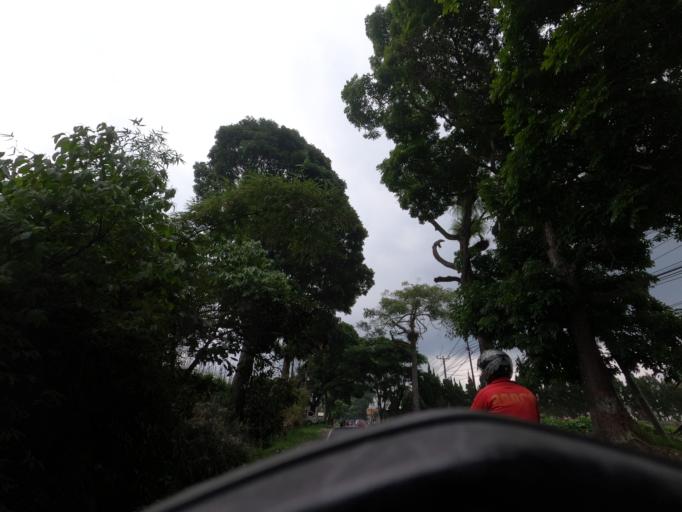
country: ID
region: West Java
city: Sukabumi
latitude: -6.7678
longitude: 107.0574
